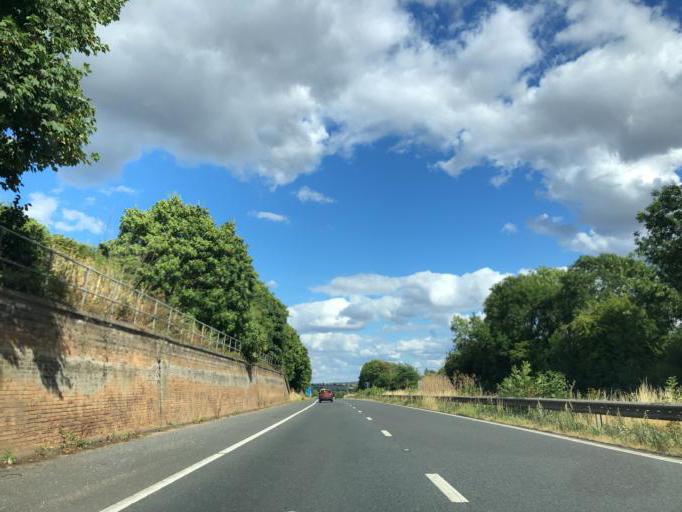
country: GB
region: England
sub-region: Warwickshire
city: Dunchurch
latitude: 52.3339
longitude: -1.2946
